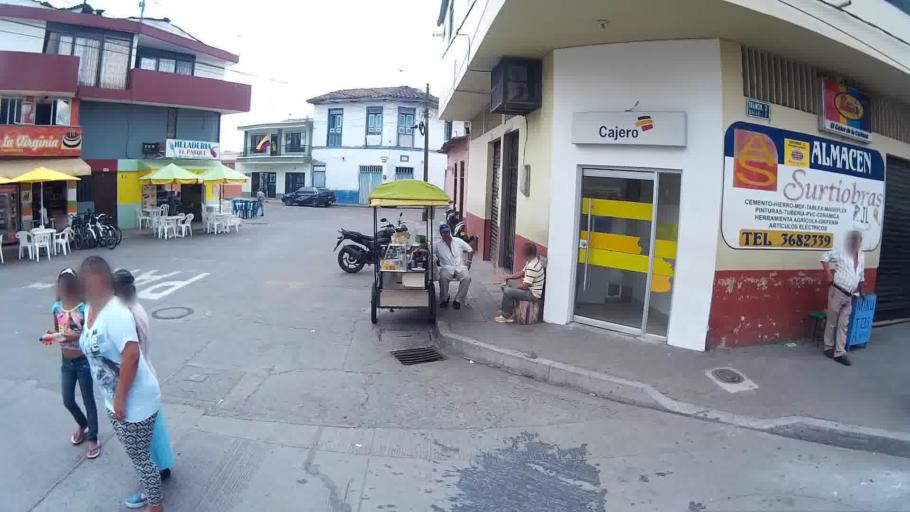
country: CO
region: Risaralda
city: La Virginia
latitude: 4.8950
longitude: -75.8837
